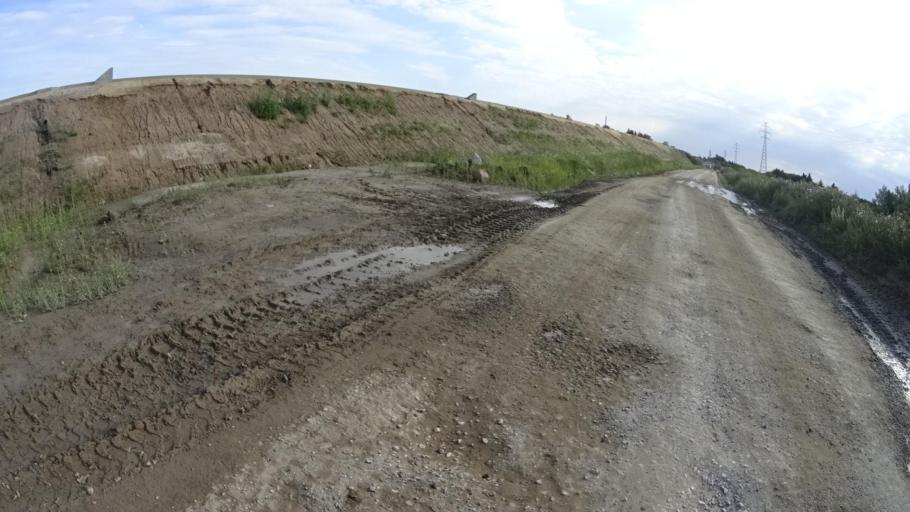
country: PL
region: Masovian Voivodeship
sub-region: Powiat piaseczynski
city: Tarczyn
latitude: 51.9888
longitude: 20.8769
